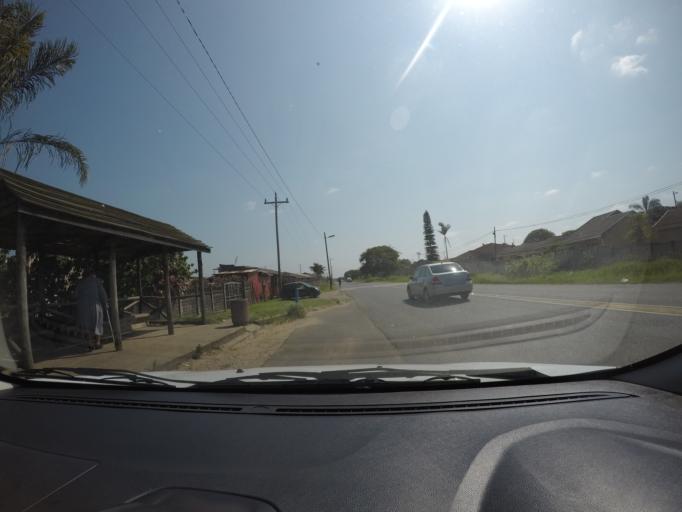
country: ZA
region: KwaZulu-Natal
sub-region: uThungulu District Municipality
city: eSikhawini
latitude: -28.8844
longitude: 31.8864
